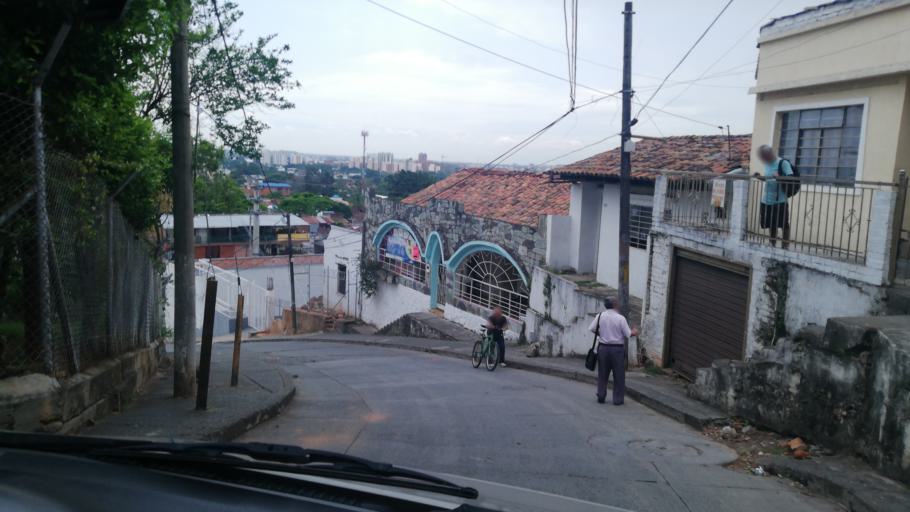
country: CO
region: Valle del Cauca
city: Cali
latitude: 3.4254
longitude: -76.5530
